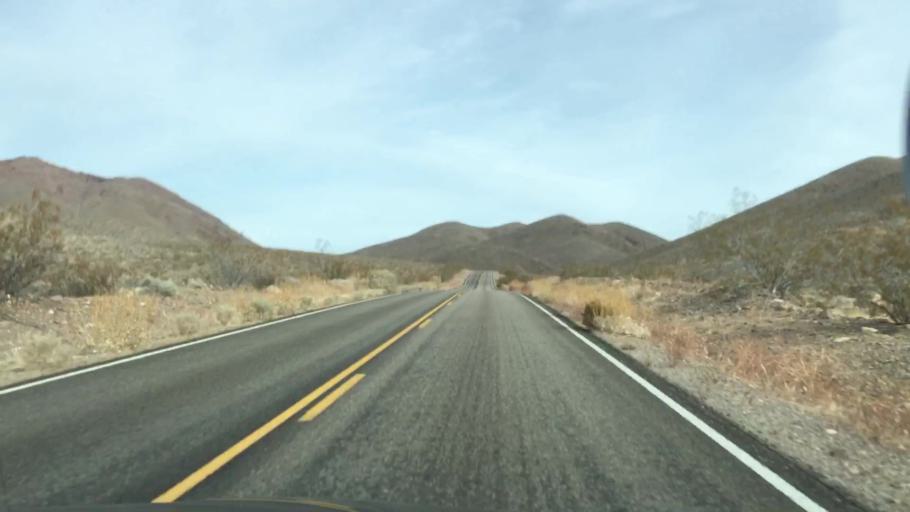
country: US
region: Nevada
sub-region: Nye County
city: Beatty
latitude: 36.7617
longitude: -116.9304
